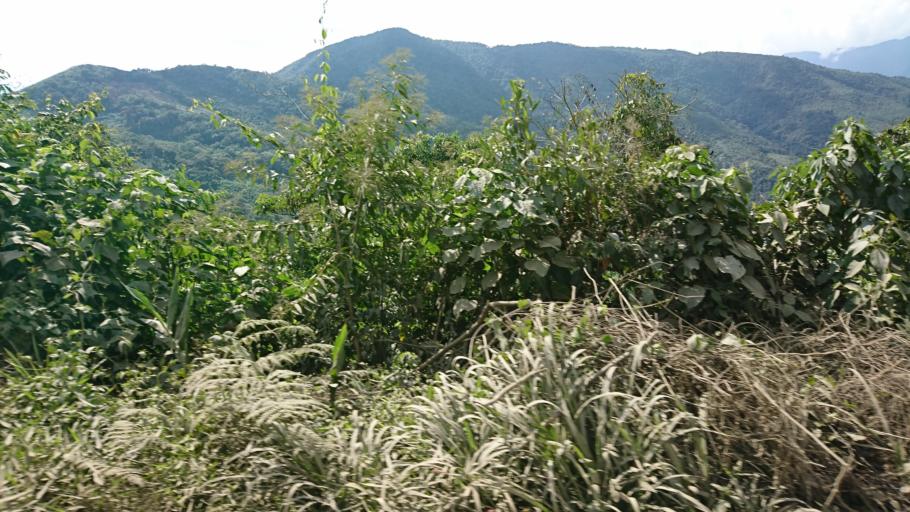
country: BO
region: La Paz
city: Coroico
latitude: -16.1350
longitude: -67.7503
